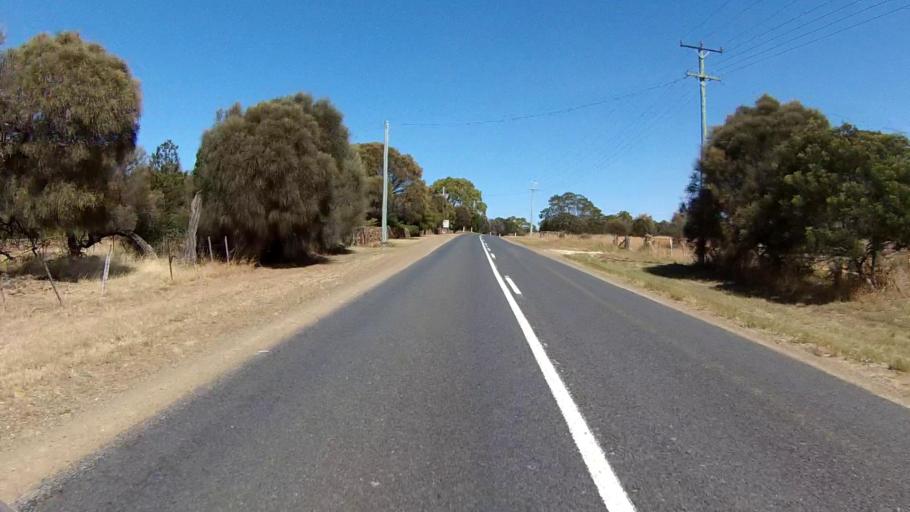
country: AU
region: Tasmania
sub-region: Sorell
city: Sorell
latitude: -42.1382
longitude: 148.0709
